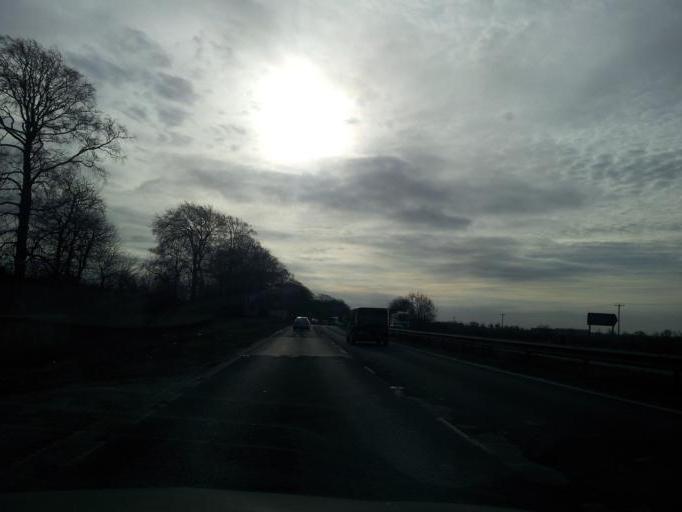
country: GB
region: England
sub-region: Lincolnshire
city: Stamford
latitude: 52.6272
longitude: -0.4663
